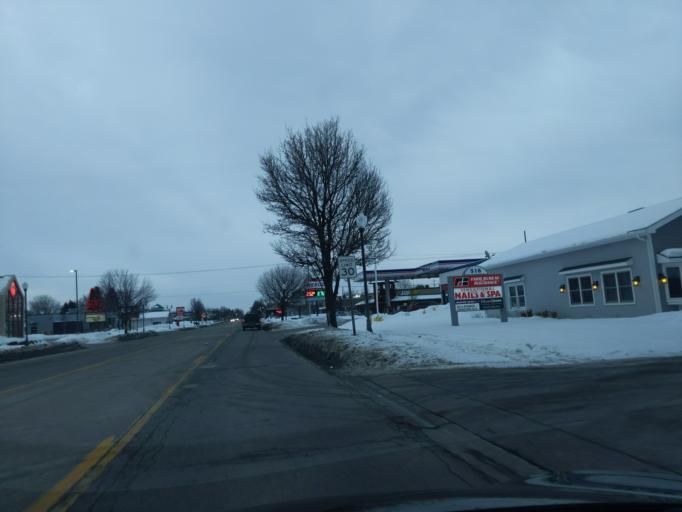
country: US
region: Michigan
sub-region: Ottawa County
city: Spring Lake
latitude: 43.0767
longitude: -86.2043
